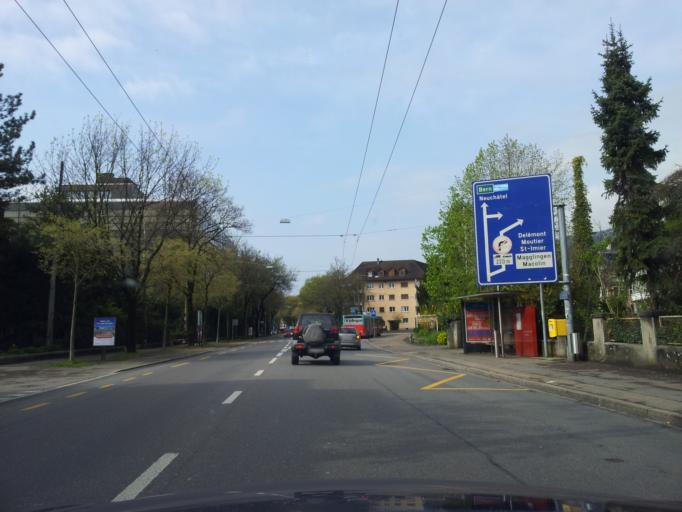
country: CH
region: Bern
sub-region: Biel/Bienne District
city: Biel/Bienne
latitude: 47.1463
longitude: 7.2544
